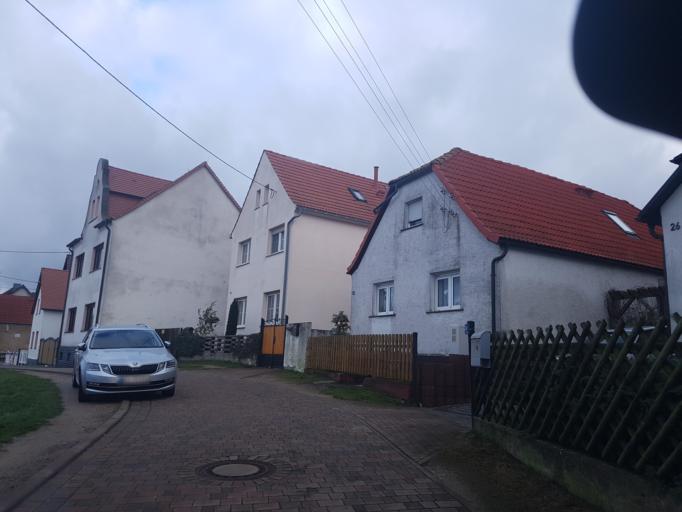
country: DE
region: Brandenburg
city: Muhlberg
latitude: 51.4039
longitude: 13.2540
